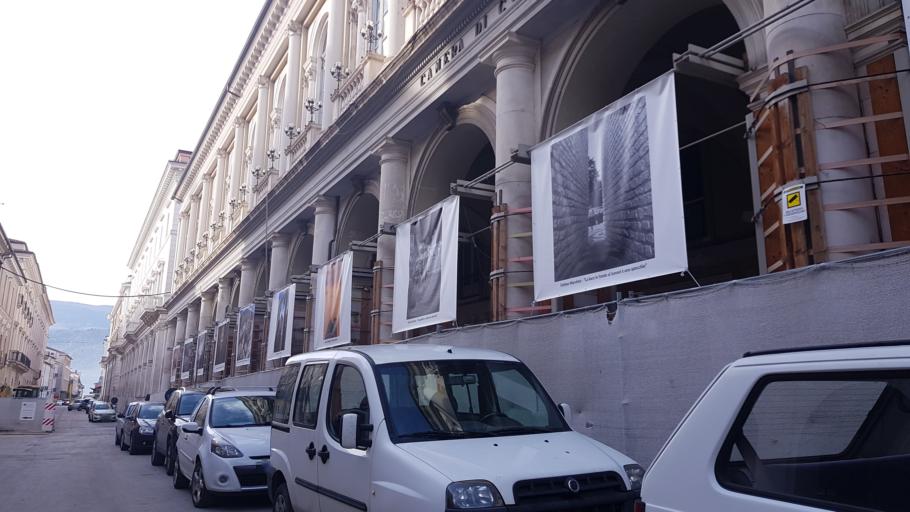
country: IT
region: Abruzzo
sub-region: Provincia dell' Aquila
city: L'Aquila
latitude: 42.3503
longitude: 13.3997
